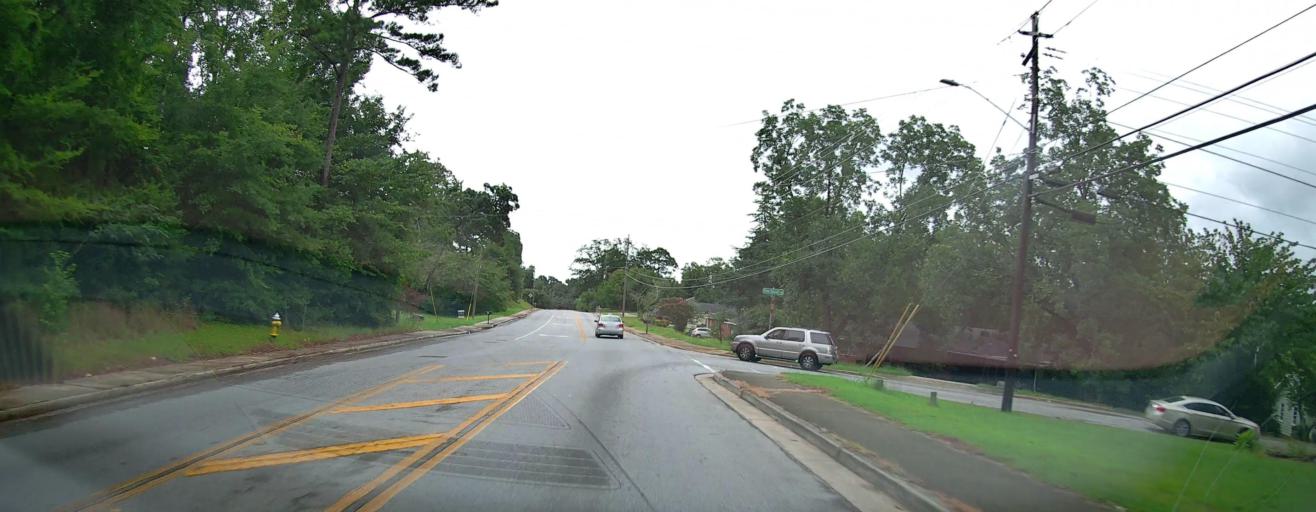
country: US
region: Georgia
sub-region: Bibb County
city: Macon
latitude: 32.7982
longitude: -83.6993
